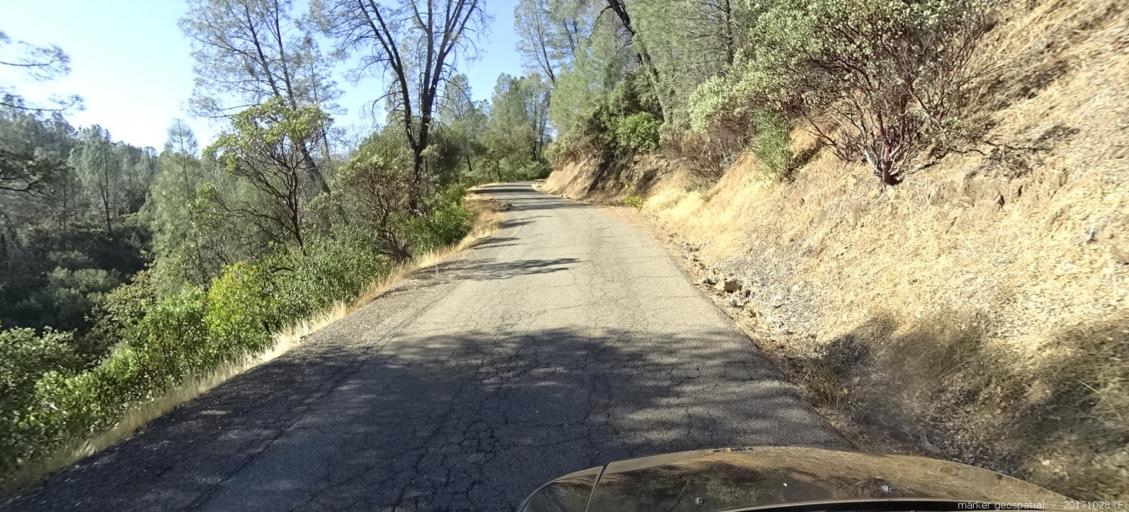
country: US
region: California
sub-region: Shasta County
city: Shasta
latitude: 40.5950
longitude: -122.4610
